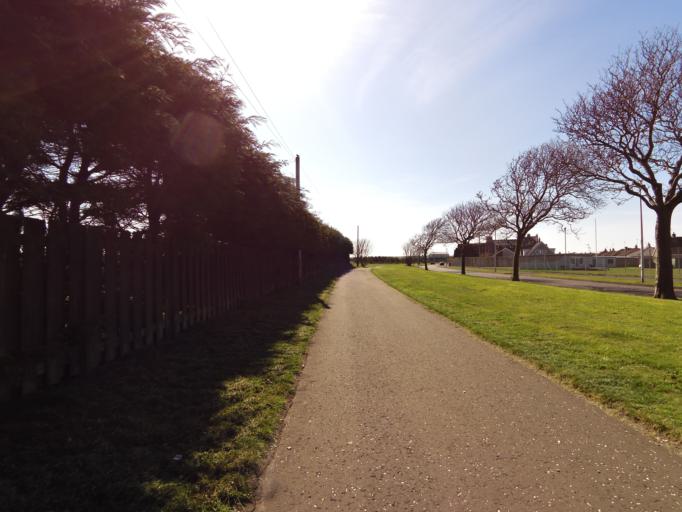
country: GB
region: Scotland
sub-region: Angus
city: Montrose
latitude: 56.7142
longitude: -2.4542
